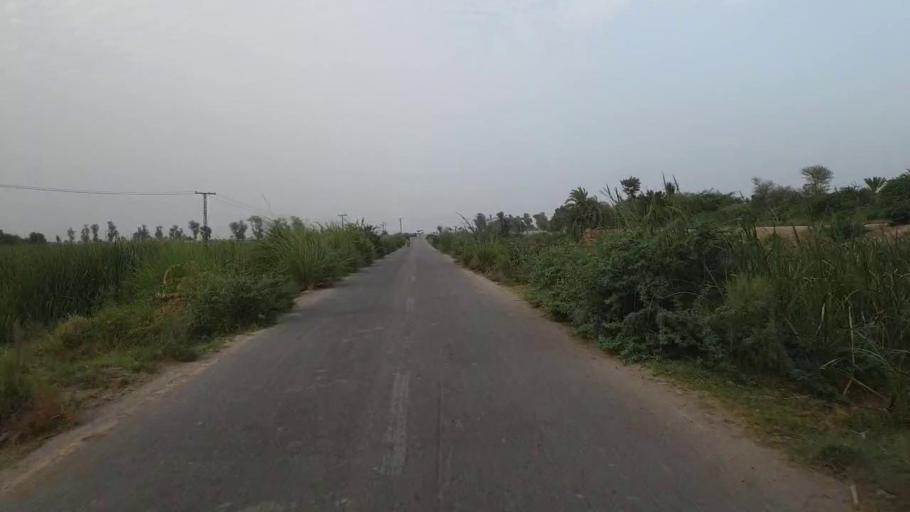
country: PK
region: Sindh
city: Daur
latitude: 26.4548
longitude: 68.2930
